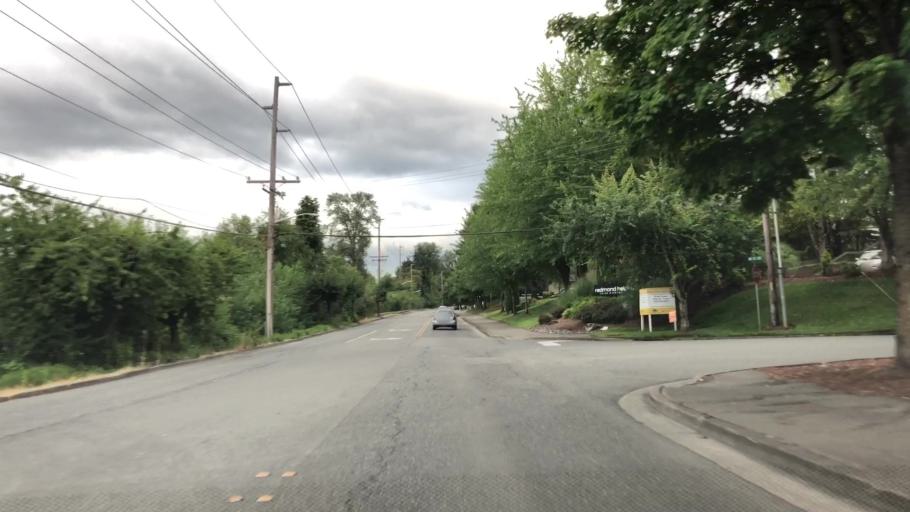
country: US
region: Washington
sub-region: King County
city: Redmond
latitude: 47.6807
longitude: -122.1409
